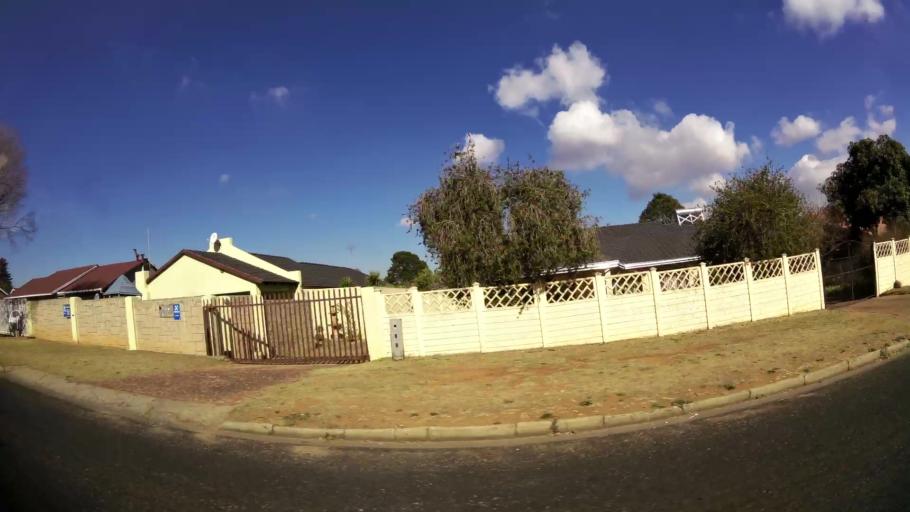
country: ZA
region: Gauteng
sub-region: City of Johannesburg Metropolitan Municipality
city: Roodepoort
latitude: -26.1416
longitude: 27.8252
